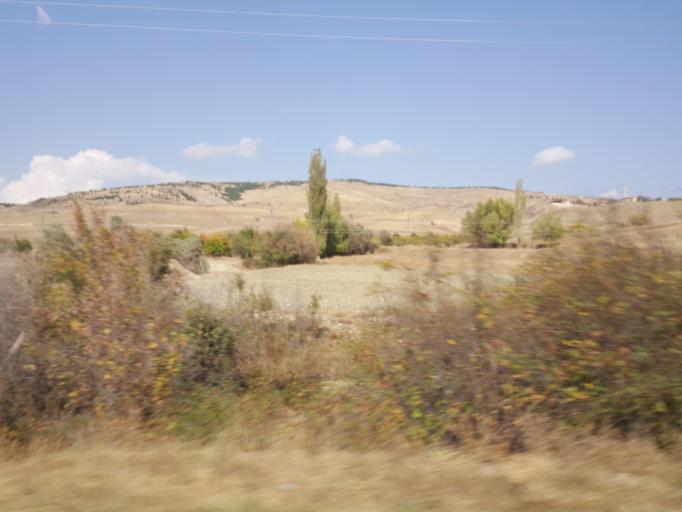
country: TR
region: Corum
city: Bogazkale
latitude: 40.1592
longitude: 34.6318
